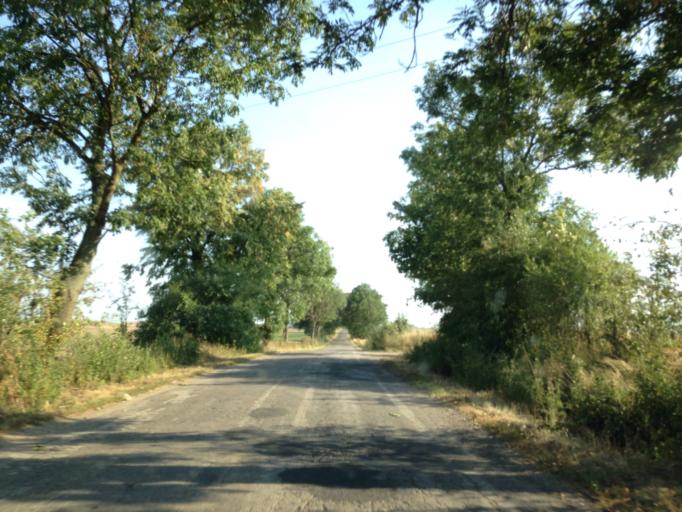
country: PL
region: Kujawsko-Pomorskie
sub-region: Powiat grudziadzki
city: Lasin
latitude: 53.5382
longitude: 19.1379
